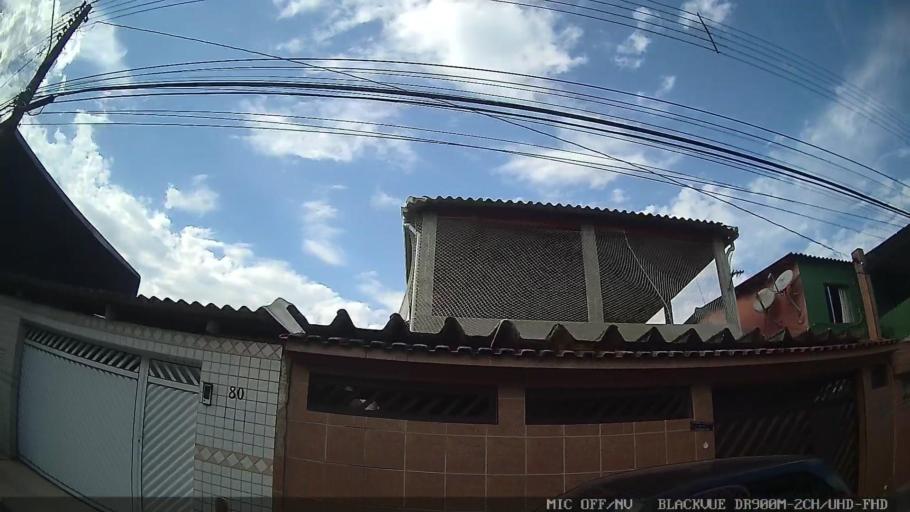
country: BR
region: Sao Paulo
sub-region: Guaruja
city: Guaruja
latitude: -23.9616
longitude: -46.2533
